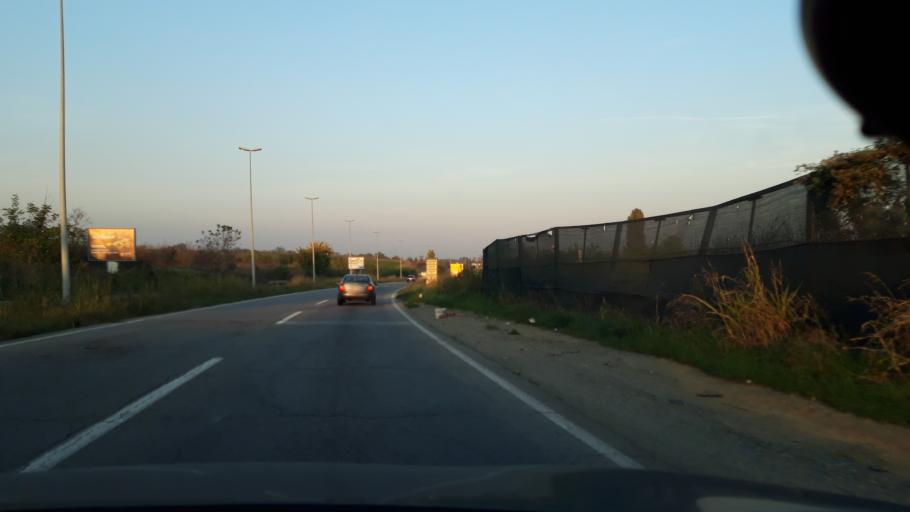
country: RS
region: Autonomna Pokrajina Vojvodina
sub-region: Juznobacki Okrug
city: Petrovaradin
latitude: 45.2223
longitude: 19.8706
